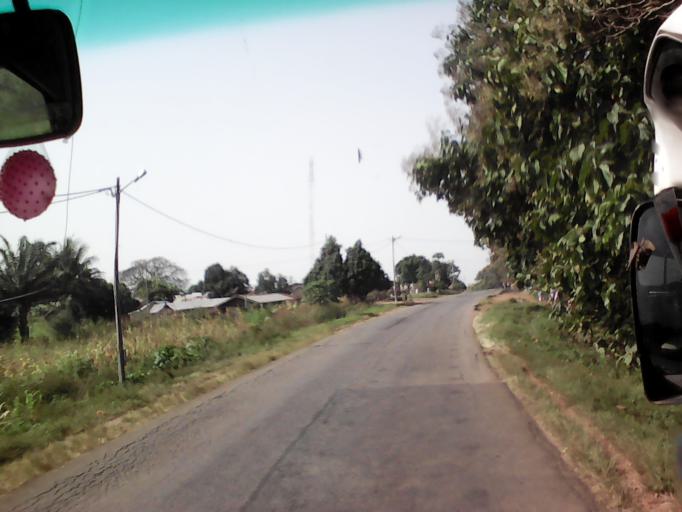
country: TG
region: Centrale
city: Sokode
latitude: 9.1387
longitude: 1.1536
